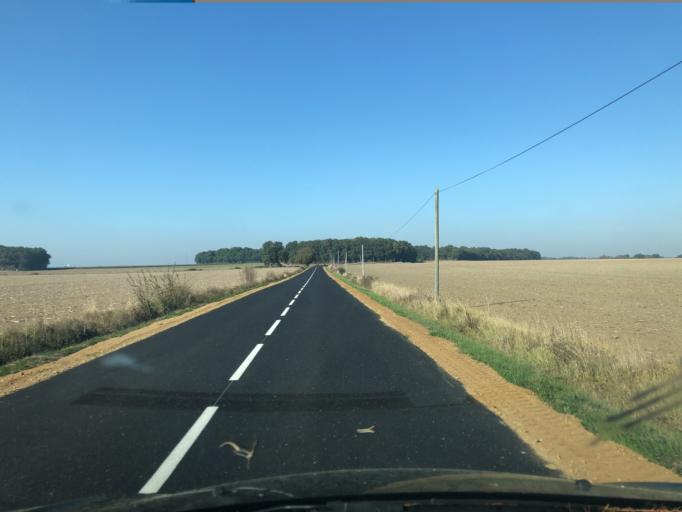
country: FR
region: Centre
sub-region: Departement d'Indre-et-Loire
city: Rouziers-de-Touraine
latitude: 47.5477
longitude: 0.6173
